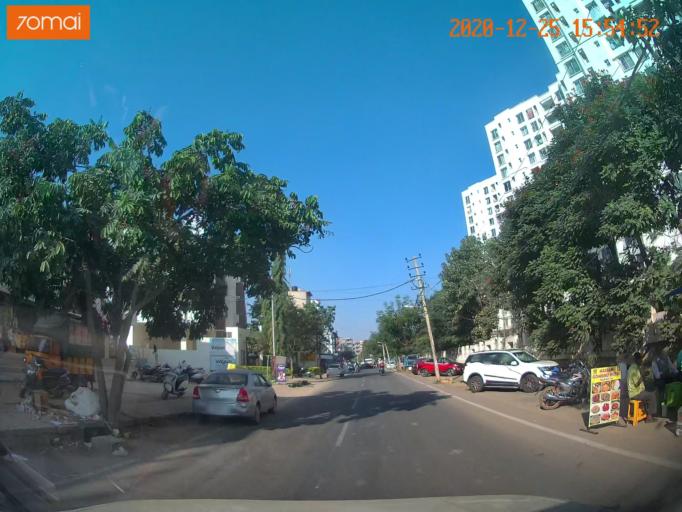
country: IN
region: Karnataka
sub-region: Bangalore Urban
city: Bangalore
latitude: 12.8589
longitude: 77.6120
